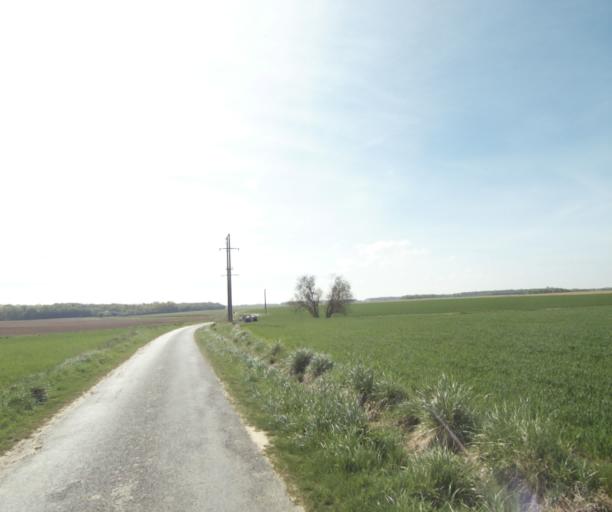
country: FR
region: Ile-de-France
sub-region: Departement de Seine-et-Marne
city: Nangis
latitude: 48.5475
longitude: 3.0350
